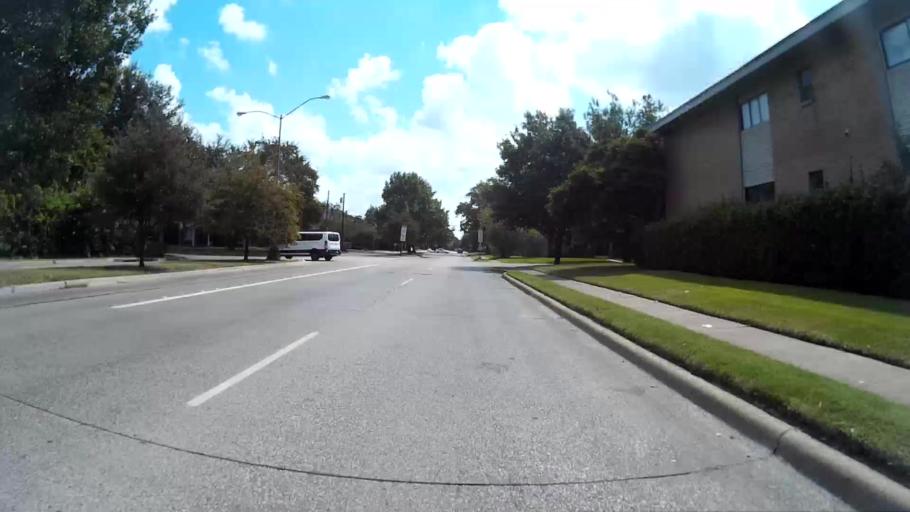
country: US
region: Texas
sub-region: Dallas County
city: Highland Park
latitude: 32.8023
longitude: -96.7653
